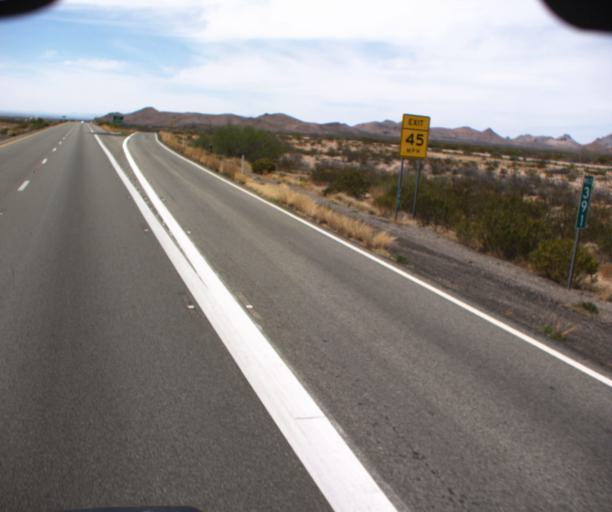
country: US
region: New Mexico
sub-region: Hidalgo County
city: Lordsburg
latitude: 32.2285
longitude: -109.0517
